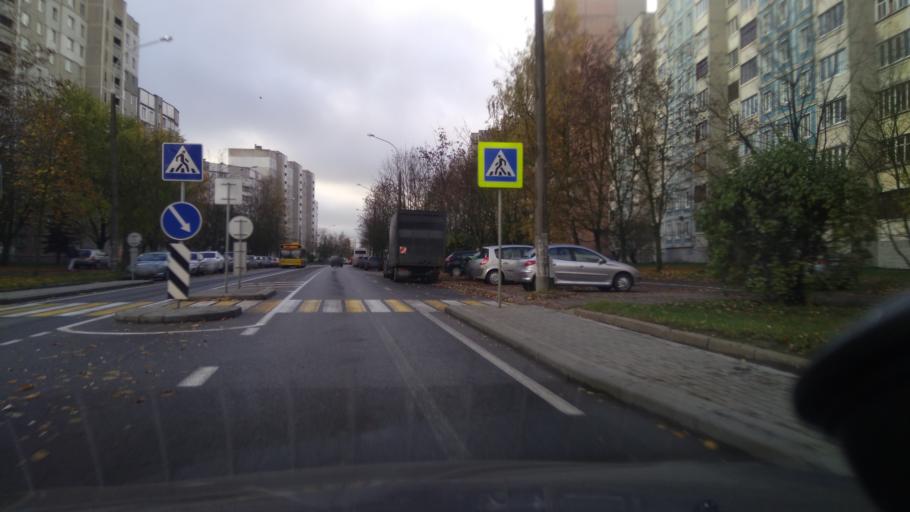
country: BY
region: Minsk
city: Malinovka
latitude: 53.8589
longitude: 27.4362
